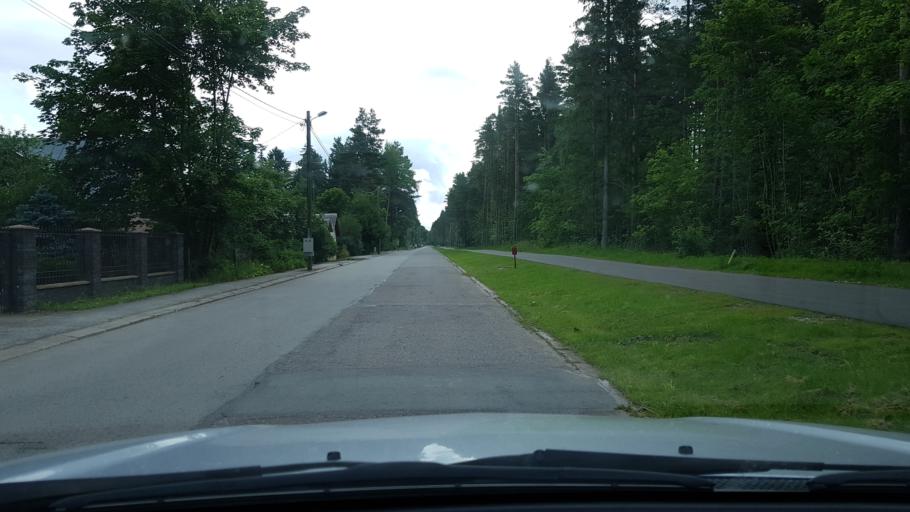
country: EE
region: Ida-Virumaa
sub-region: Narva-Joesuu linn
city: Narva-Joesuu
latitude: 59.4473
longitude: 28.0273
